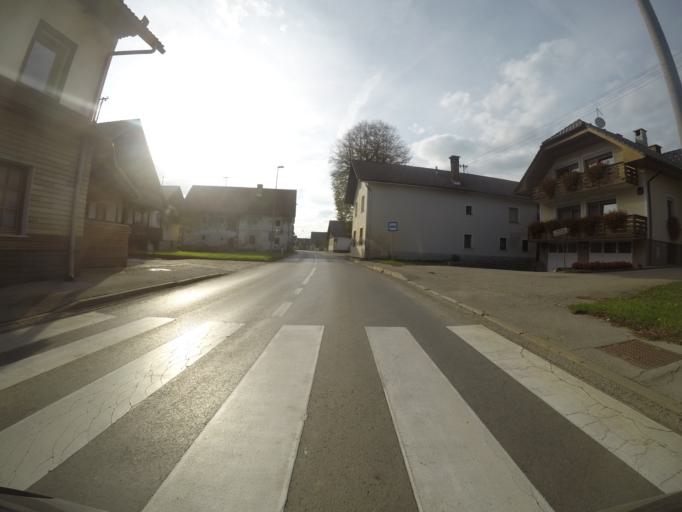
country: SI
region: Vodice
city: Vodice
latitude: 46.1796
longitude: 14.4667
